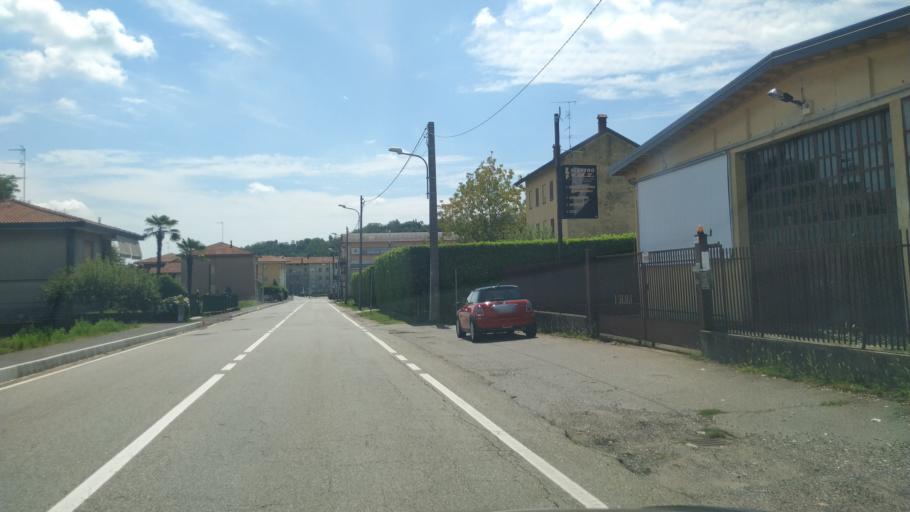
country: IT
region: Piedmont
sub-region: Provincia di Novara
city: Borgomanero
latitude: 45.7018
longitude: 8.4475
